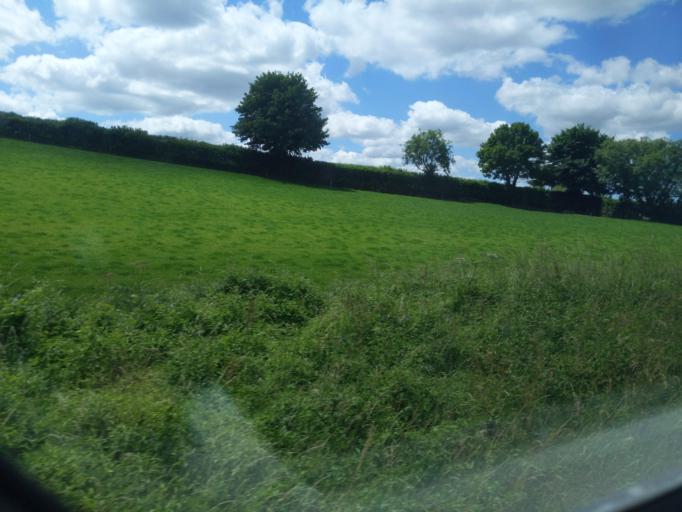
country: GB
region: England
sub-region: Cornwall
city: Liskeard
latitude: 50.4302
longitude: -4.4178
